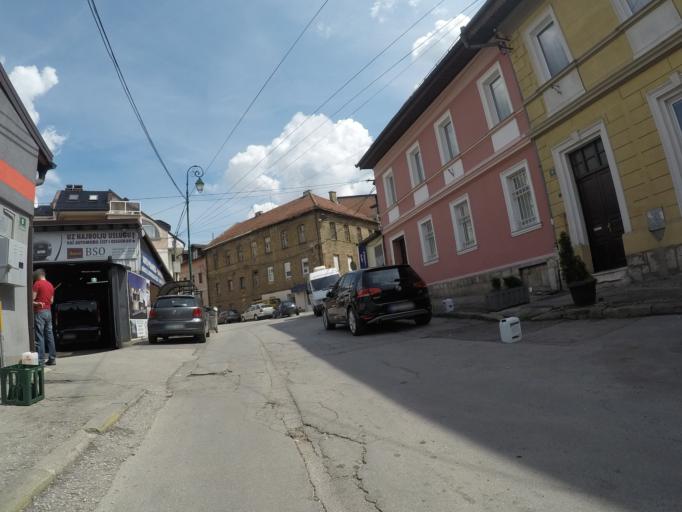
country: BA
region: Federation of Bosnia and Herzegovina
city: Kobilja Glava
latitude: 43.8561
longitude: 18.4335
